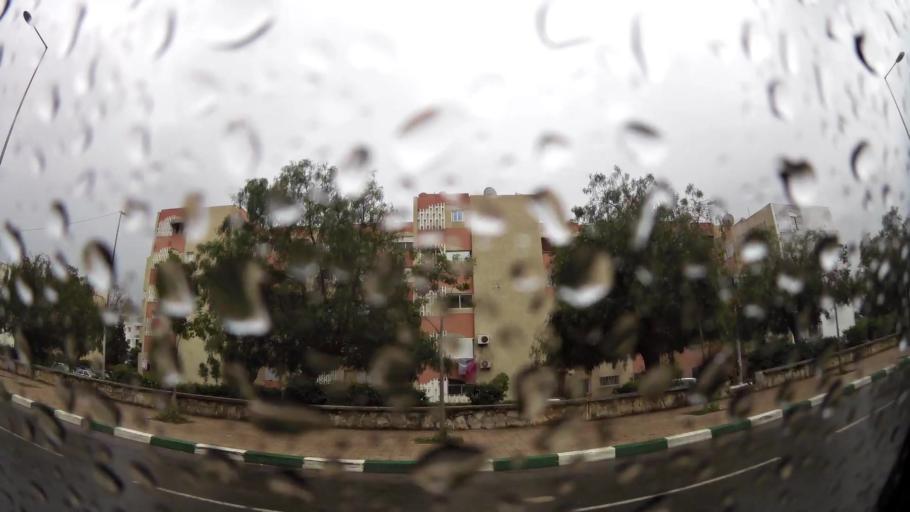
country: MA
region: Grand Casablanca
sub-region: Mediouna
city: Tit Mellil
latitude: 33.6165
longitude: -7.4829
